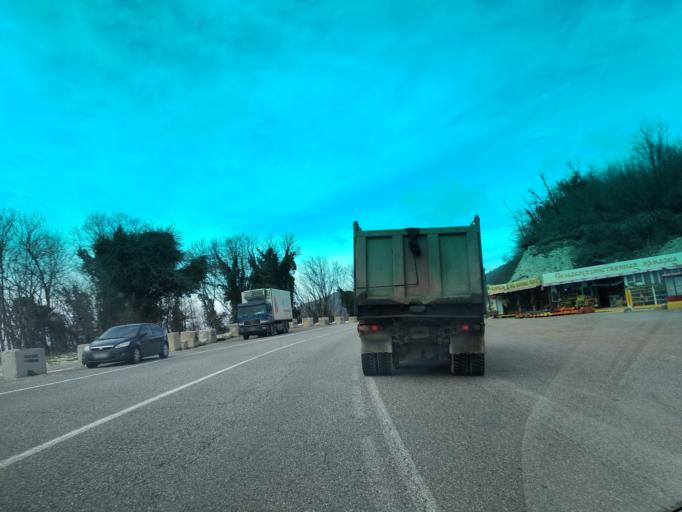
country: RU
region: Krasnodarskiy
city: Shepsi
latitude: 44.0718
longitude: 39.1354
